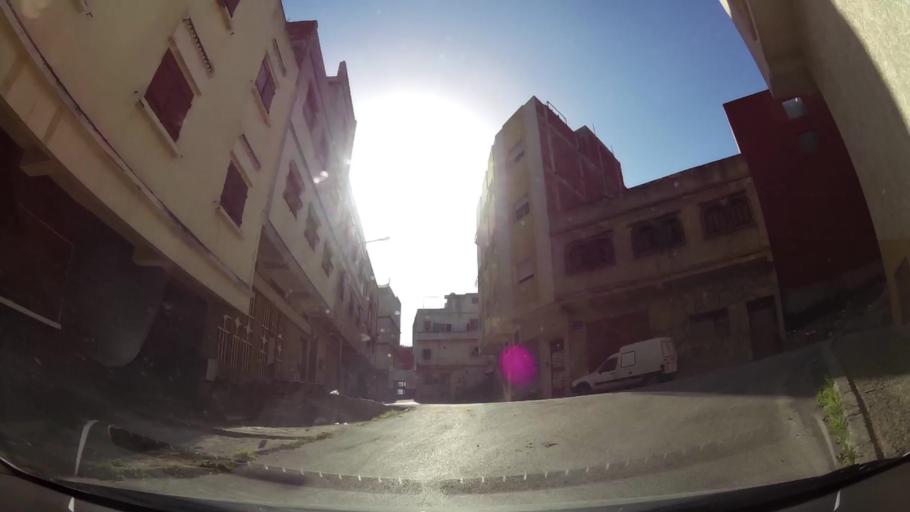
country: MA
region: Tanger-Tetouan
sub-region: Tanger-Assilah
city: Tangier
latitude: 35.7438
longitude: -5.8038
